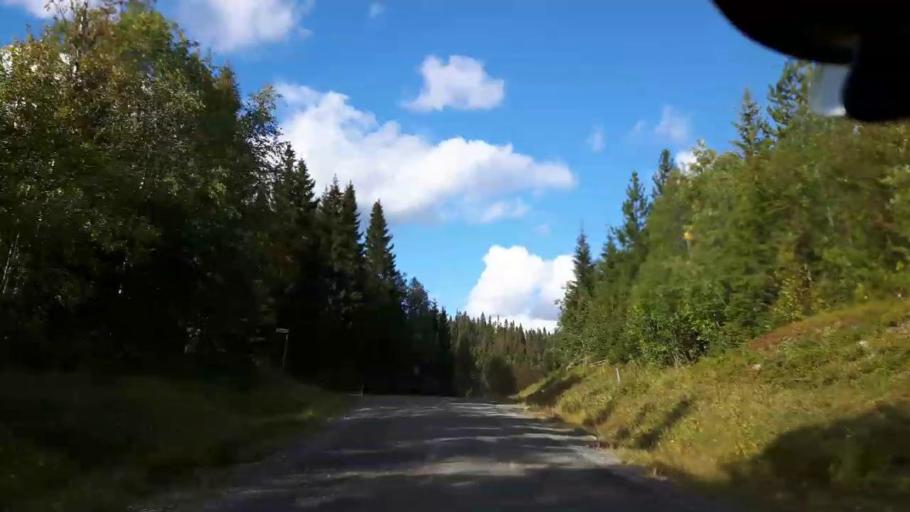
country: SE
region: Jaemtland
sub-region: Ragunda Kommun
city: Hammarstrand
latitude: 63.4114
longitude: 16.0930
